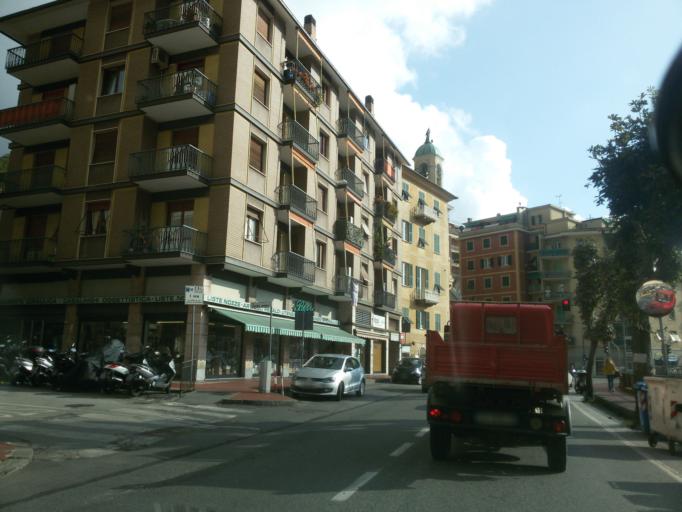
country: IT
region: Liguria
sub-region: Provincia di Genova
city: Recco
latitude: 44.3652
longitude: 9.1468
